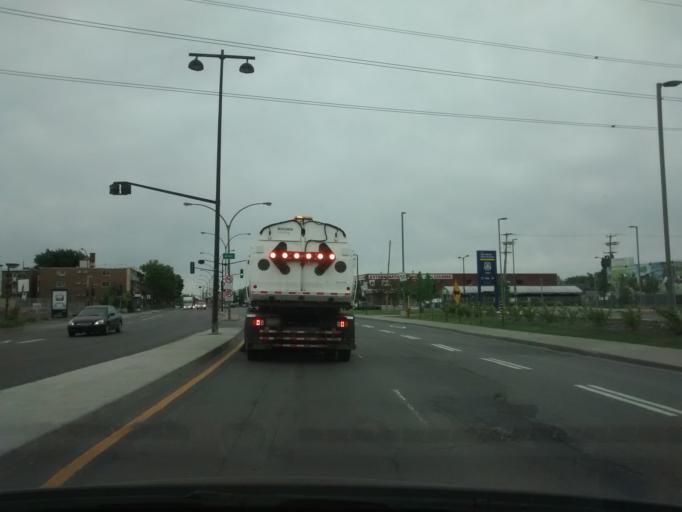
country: CA
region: Quebec
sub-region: Montreal
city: Saint-Leonard
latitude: 45.5833
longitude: -73.6293
